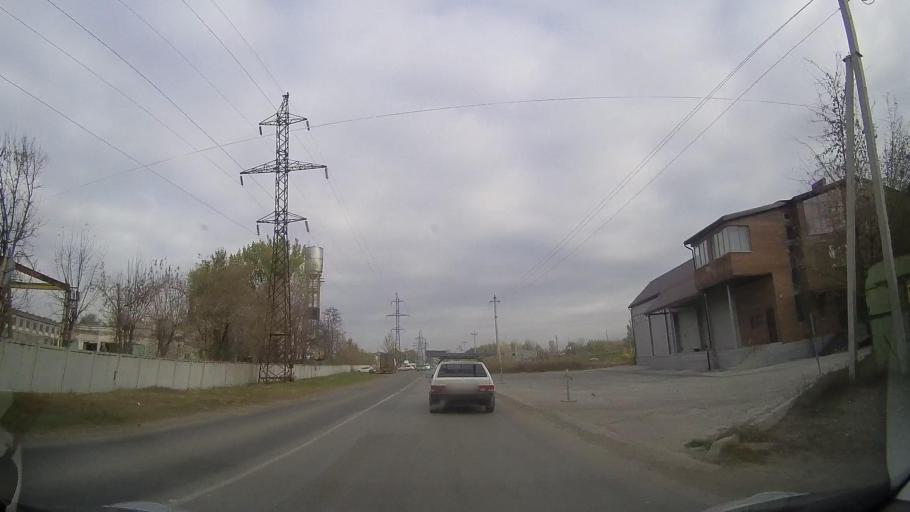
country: RU
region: Rostov
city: Bataysk
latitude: 47.1066
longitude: 39.7631
